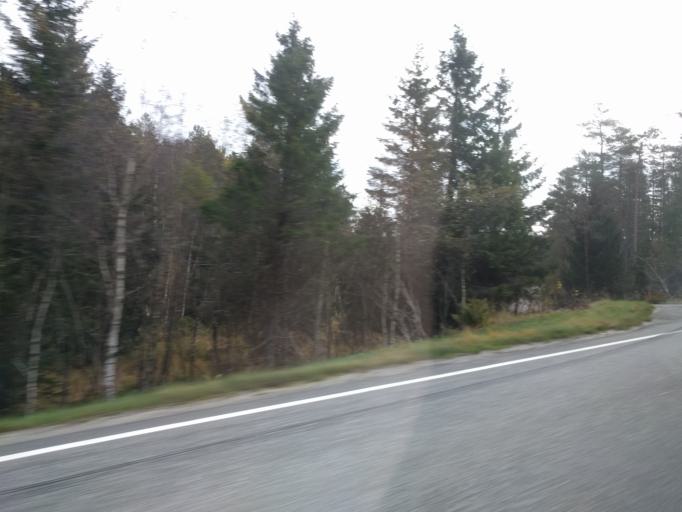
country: NO
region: Vest-Agder
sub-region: Songdalen
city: Nodeland
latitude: 58.3129
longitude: 7.8061
